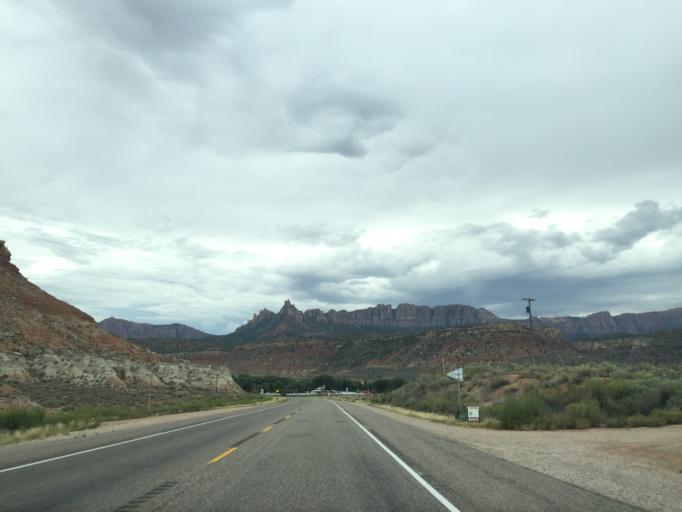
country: US
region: Utah
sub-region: Washington County
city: Hildale
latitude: 37.1654
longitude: -113.0618
